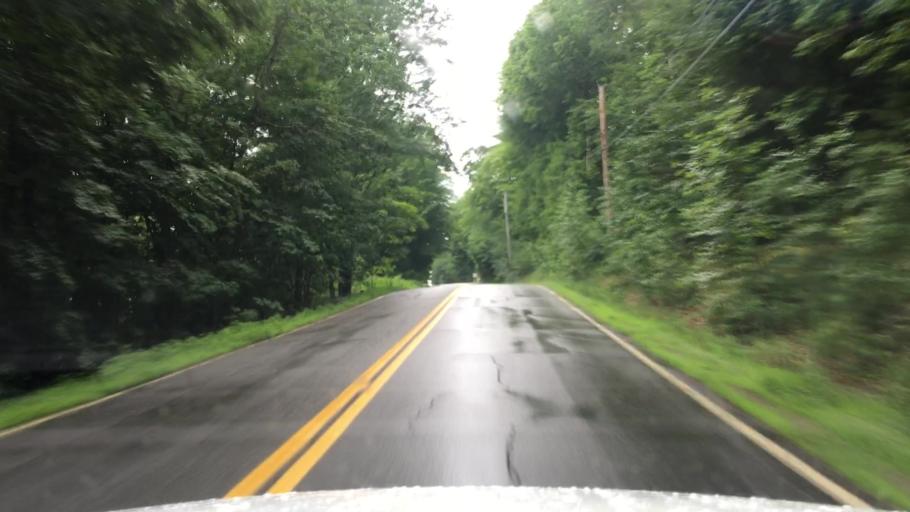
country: US
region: Maine
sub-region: Kennebec County
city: Winthrop
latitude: 44.2987
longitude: -69.9264
